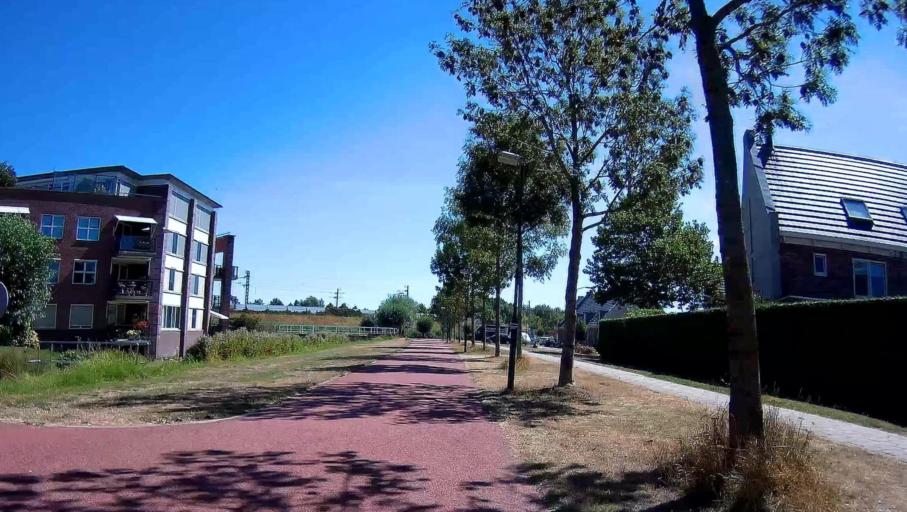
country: NL
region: Utrecht
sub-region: Gemeente Houten
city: Houten
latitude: 52.0117
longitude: 5.1803
